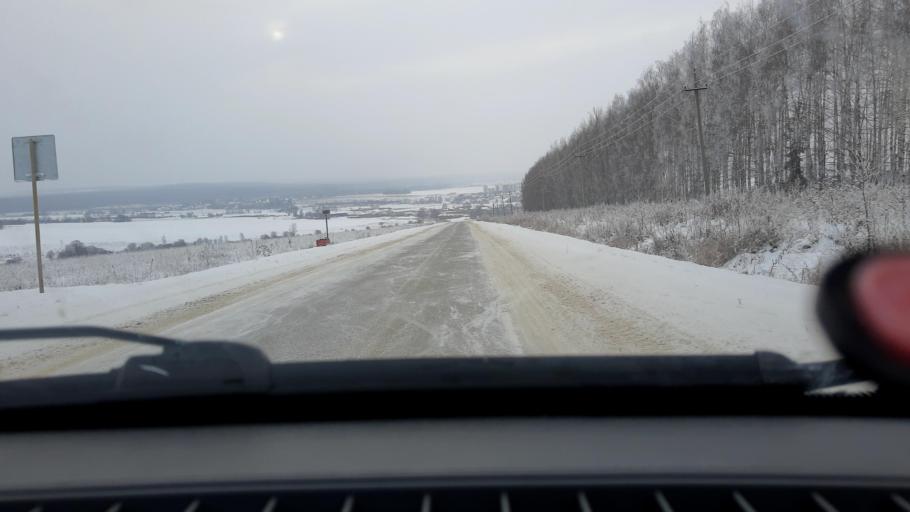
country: RU
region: Bashkortostan
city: Iglino
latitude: 54.6547
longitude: 56.4258
